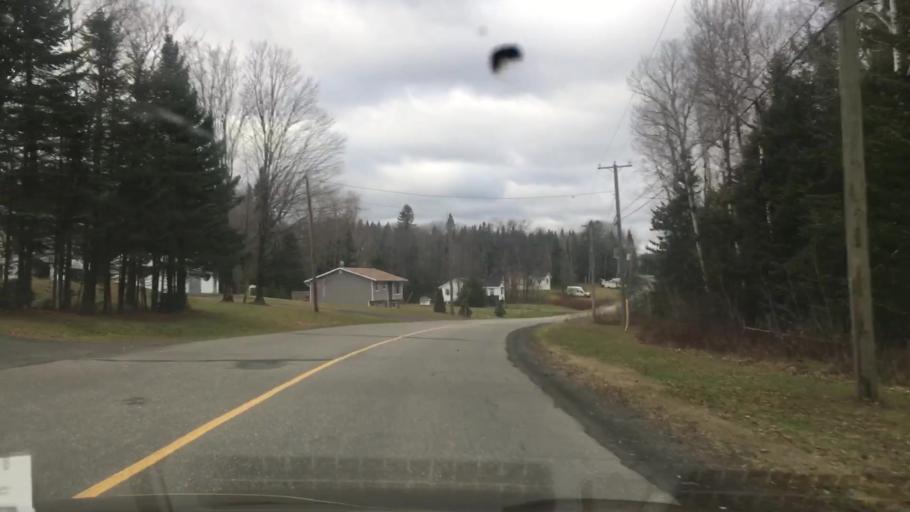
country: US
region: Maine
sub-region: Aroostook County
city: Fort Fairfield
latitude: 46.7479
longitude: -67.7478
